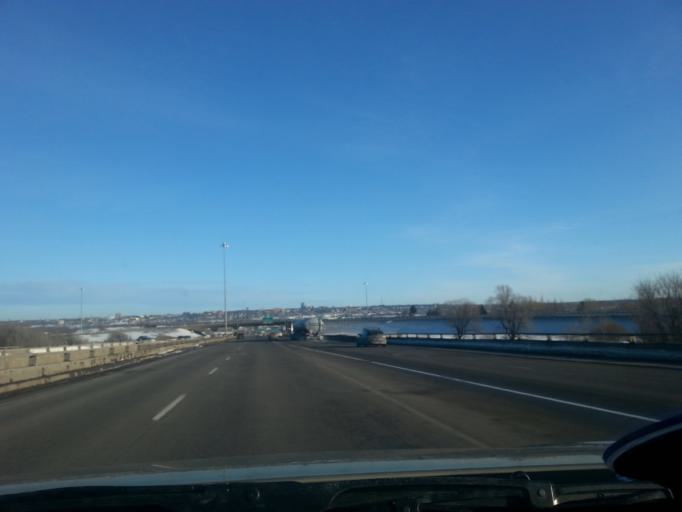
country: CA
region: Quebec
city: L'Ancienne-Lorette
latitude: 46.8118
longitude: -71.3396
